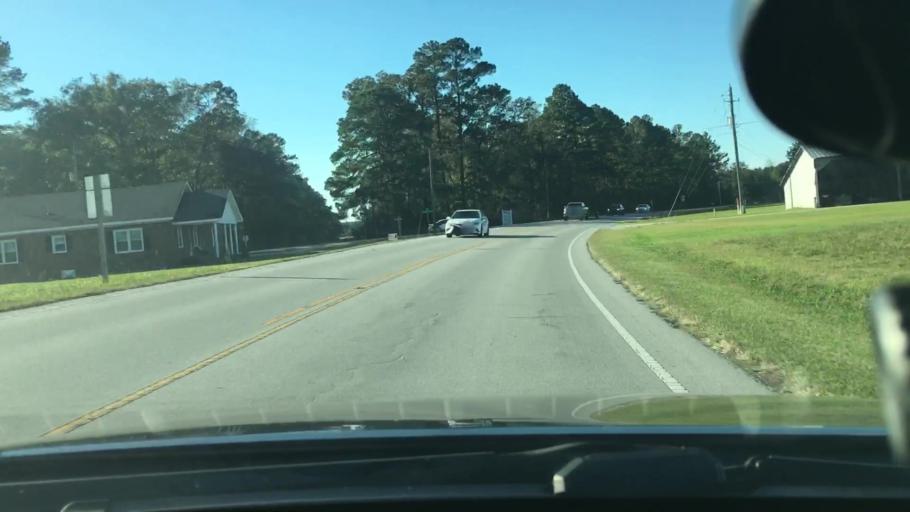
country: US
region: North Carolina
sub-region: Pitt County
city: Windsor
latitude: 35.4745
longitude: -77.2935
